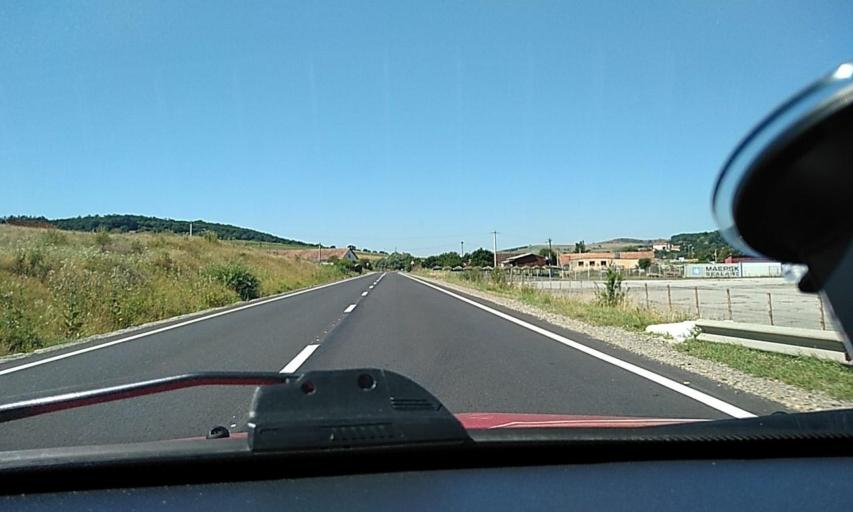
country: RO
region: Brasov
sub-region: Oras Rupea
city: Rupea
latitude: 46.0330
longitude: 25.2362
